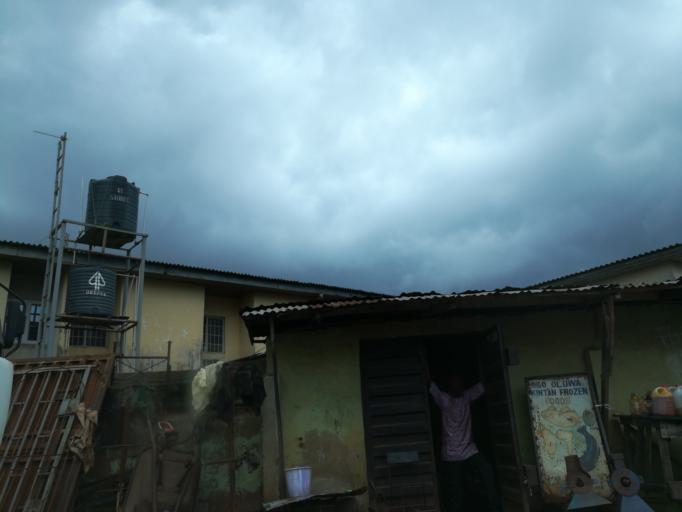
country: NG
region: Lagos
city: Agege
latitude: 6.6056
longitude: 3.3038
